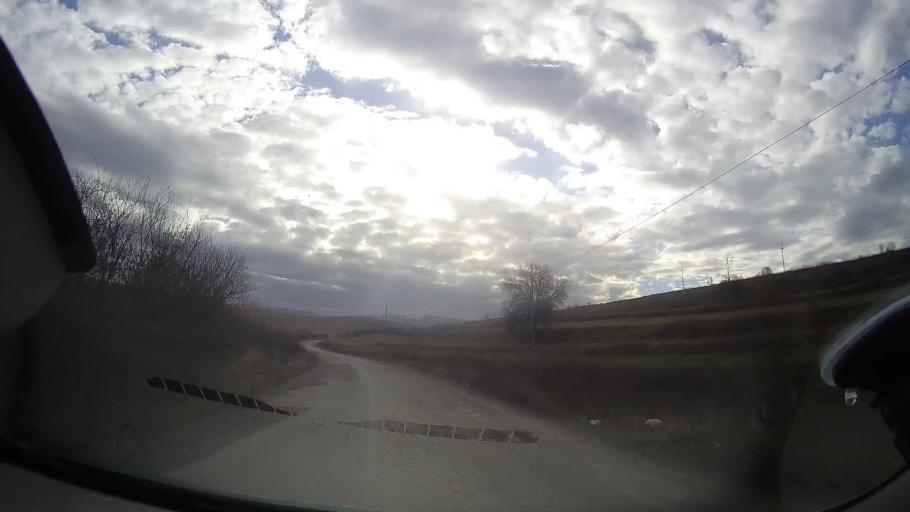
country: RO
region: Cluj
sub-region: Comuna Baisoara
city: Baisoara
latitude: 46.6080
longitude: 23.4578
